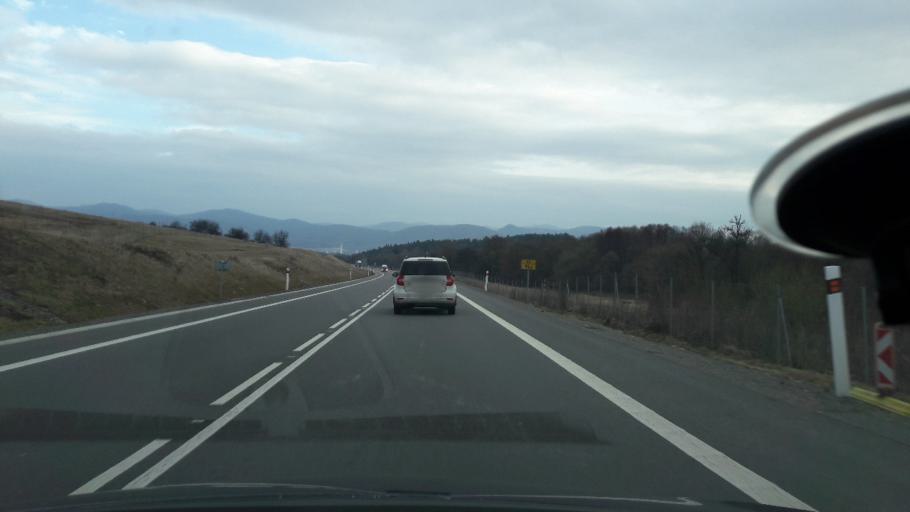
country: SK
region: Banskobystricky
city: Ziar nad Hronom
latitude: 48.6004
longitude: 18.8190
